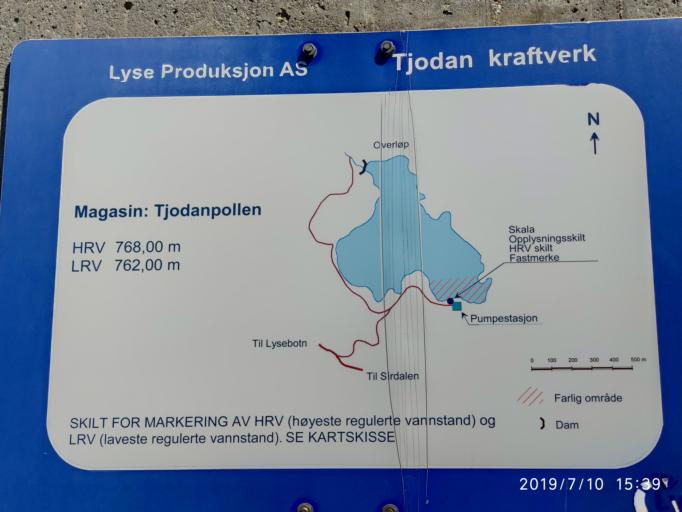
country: NO
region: Vest-Agder
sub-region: Sirdal
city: Tonstad
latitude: 59.0400
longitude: 6.7167
